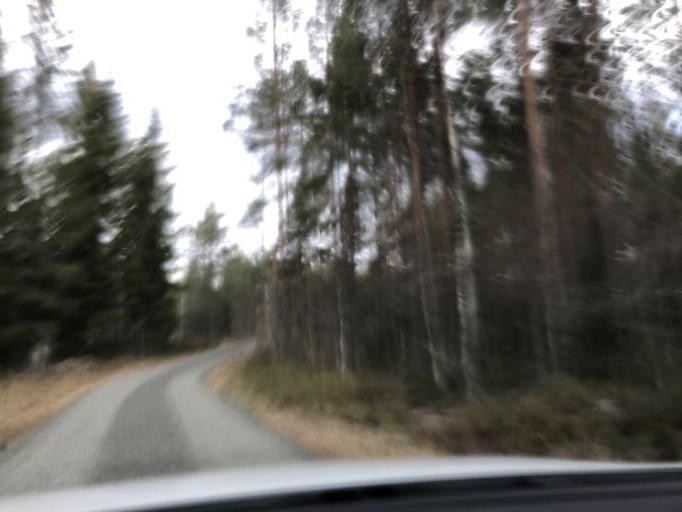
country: SE
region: Uppsala
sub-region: Heby Kommun
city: OEstervala
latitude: 60.3279
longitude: 17.1741
